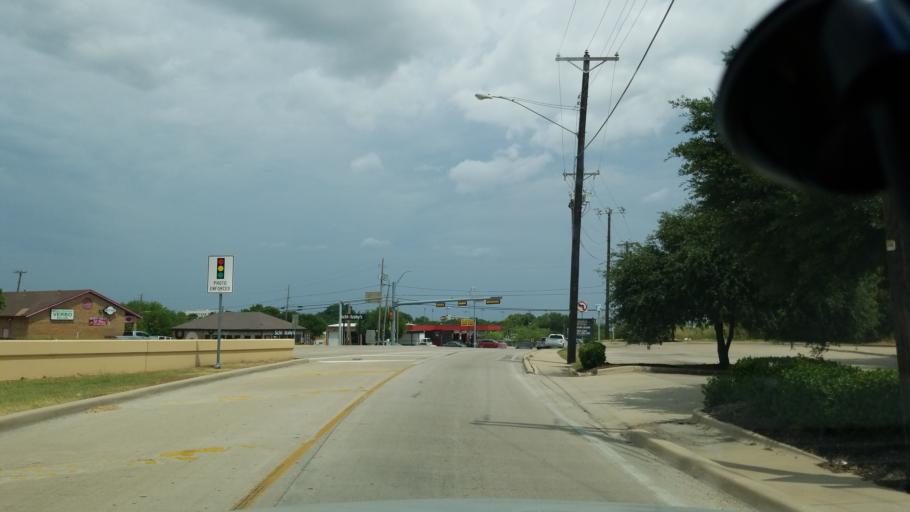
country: US
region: Texas
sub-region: Dallas County
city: Grand Prairie
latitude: 32.7478
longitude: -96.9943
